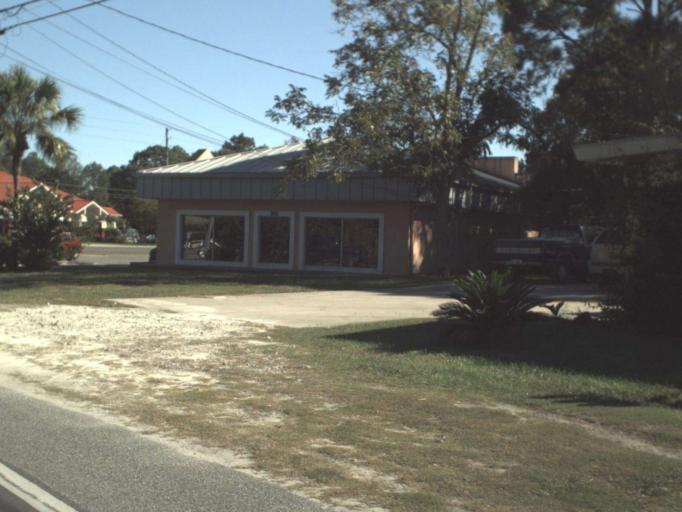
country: US
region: Florida
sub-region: Bay County
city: Panama City
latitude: 30.1787
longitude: -85.6630
